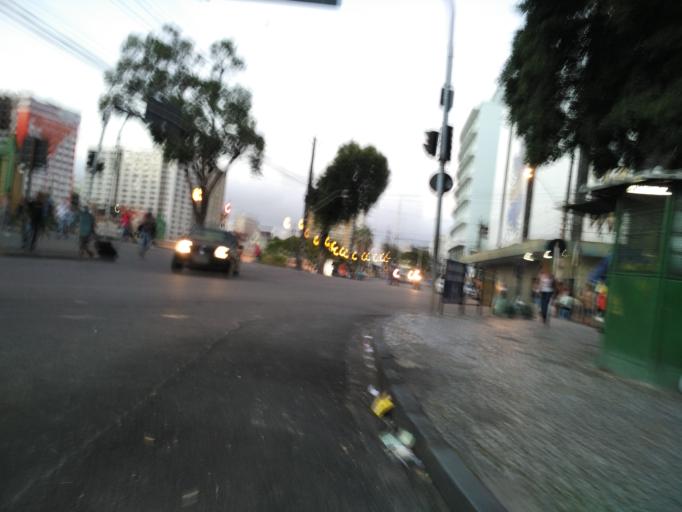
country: BR
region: Pernambuco
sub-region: Recife
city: Recife
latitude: -8.0642
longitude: -34.8810
